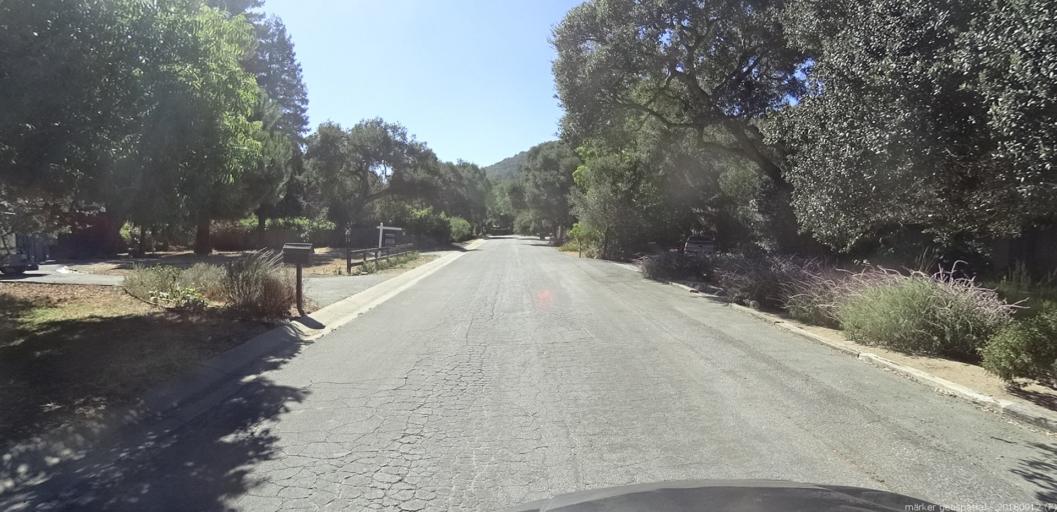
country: US
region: California
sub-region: Monterey County
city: Carmel Valley Village
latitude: 36.4938
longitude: -121.7564
